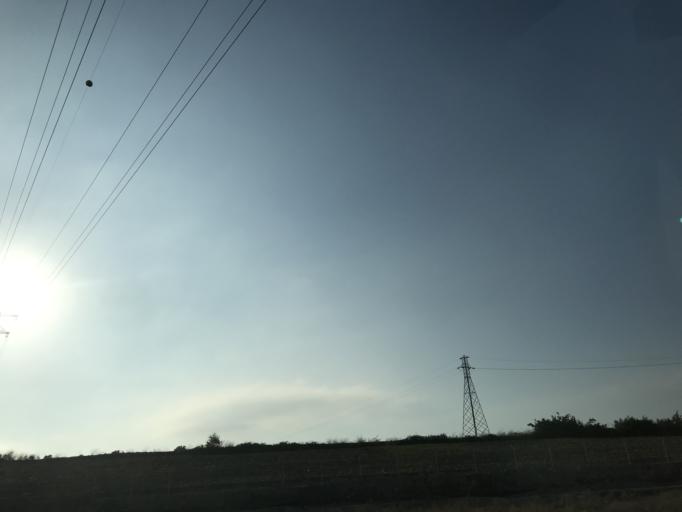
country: TR
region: Balikesir
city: Gobel
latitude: 40.0349
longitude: 28.2156
